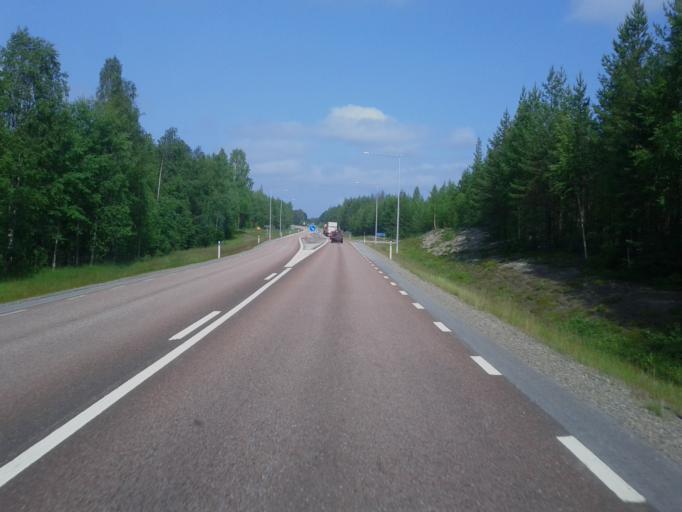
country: SE
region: Vaesterbotten
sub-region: Skelleftea Kommun
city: Burea
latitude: 64.6300
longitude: 21.1768
